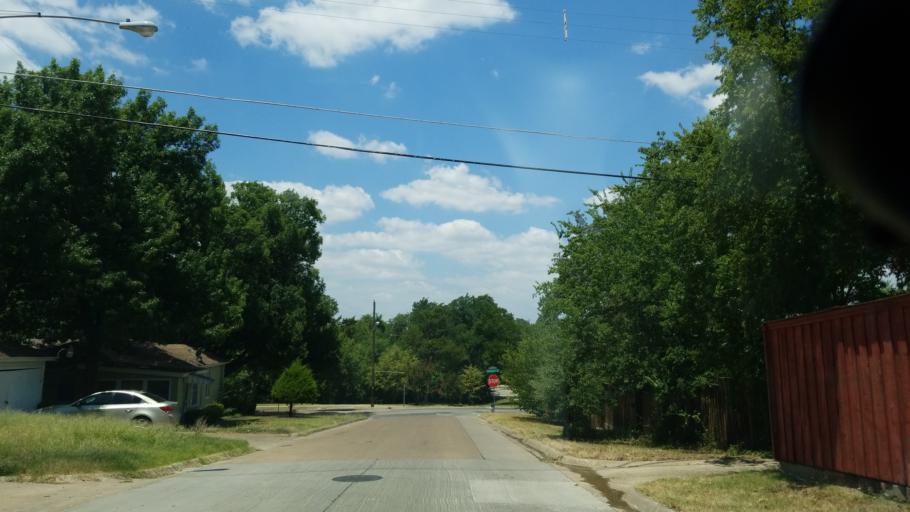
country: US
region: Texas
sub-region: Dallas County
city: Cockrell Hill
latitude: 32.7267
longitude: -96.8469
